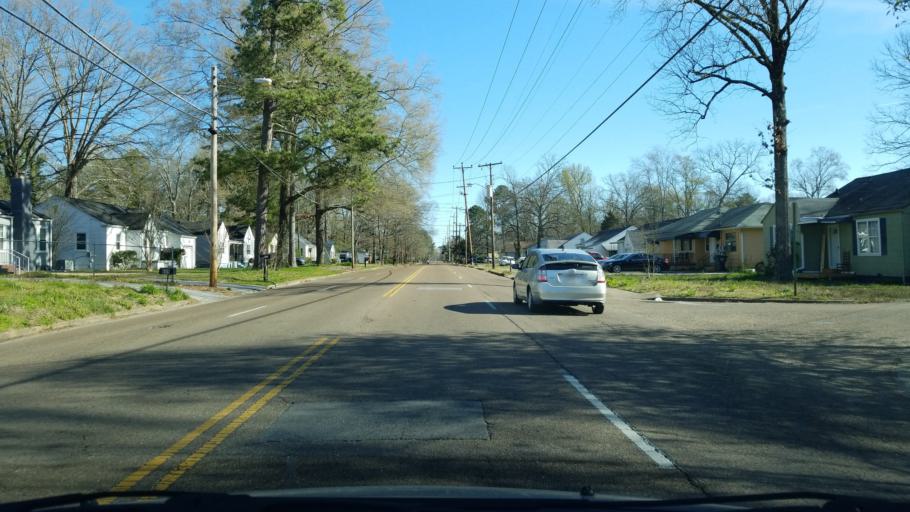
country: US
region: Tennessee
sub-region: Hamilton County
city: East Ridge
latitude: 35.0201
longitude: -85.2243
